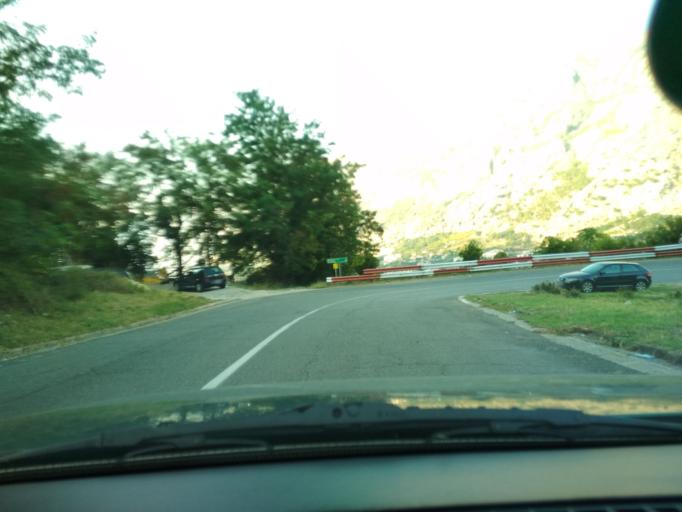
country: ME
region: Kotor
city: Kotor
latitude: 42.4219
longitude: 18.7585
